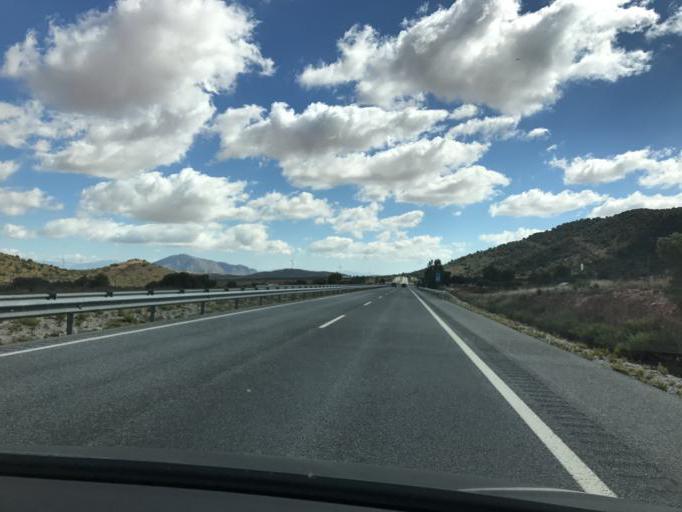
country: ES
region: Andalusia
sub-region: Provincia de Granada
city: Freila
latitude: 37.4601
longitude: -2.8723
